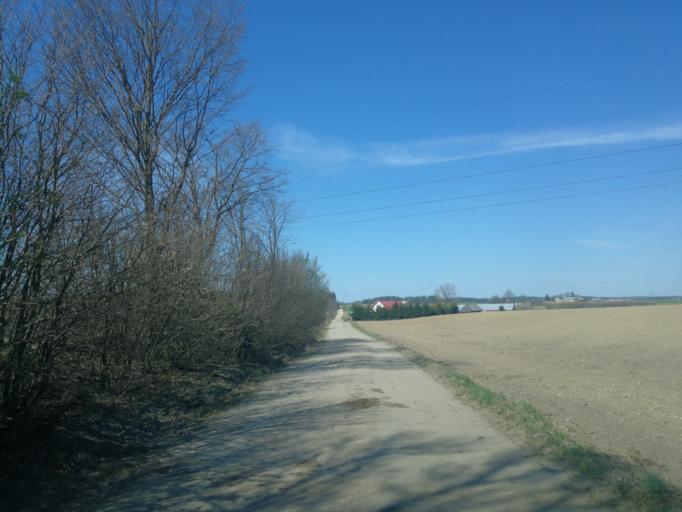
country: PL
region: Warmian-Masurian Voivodeship
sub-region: Powiat dzialdowski
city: Rybno
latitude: 53.4387
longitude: 19.9473
